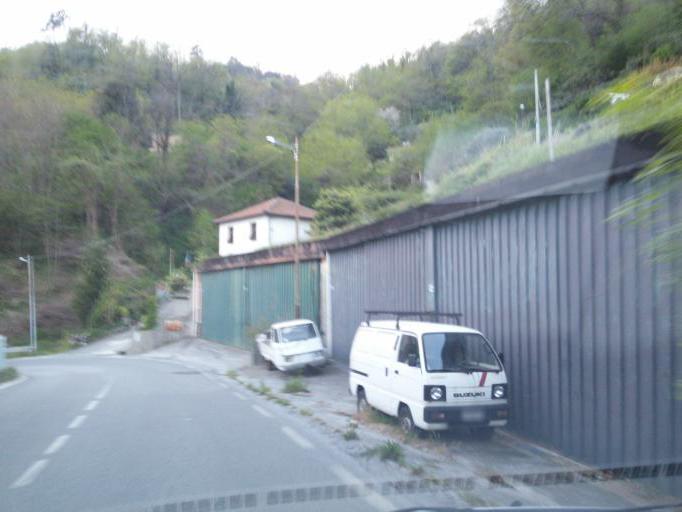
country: IT
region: Liguria
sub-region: Provincia di Genova
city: Santa Marta
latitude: 44.4794
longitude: 8.8846
